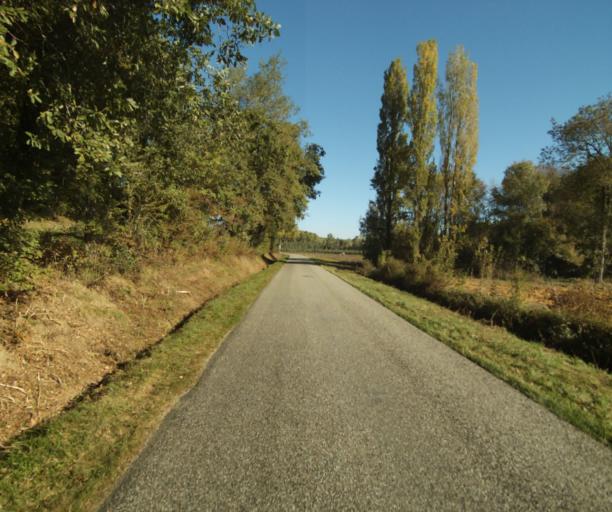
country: FR
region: Midi-Pyrenees
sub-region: Departement du Gers
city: Vic-Fezensac
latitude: 43.8247
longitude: 0.2885
